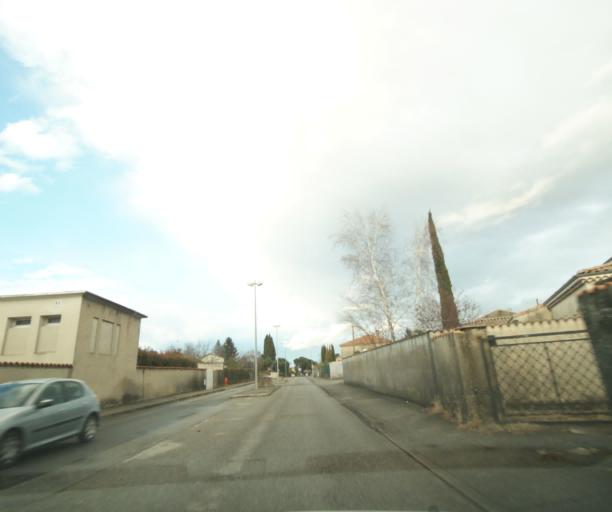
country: FR
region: Rhone-Alpes
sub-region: Departement de la Drome
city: Valence
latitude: 44.9440
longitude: 4.9060
